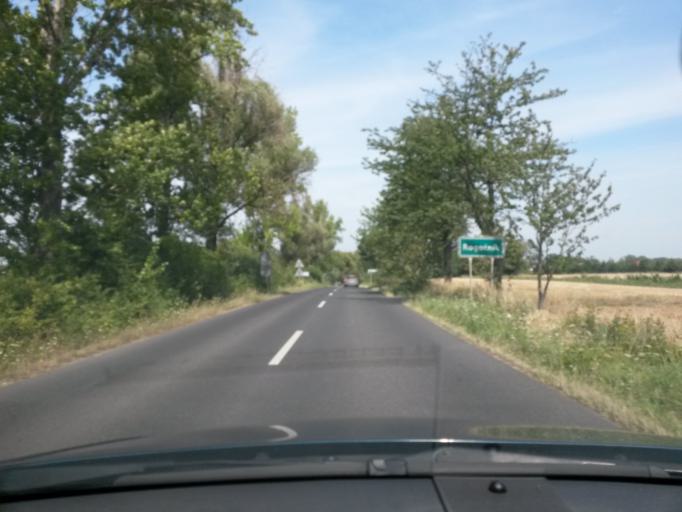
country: PL
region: Lower Silesian Voivodeship
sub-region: Powiat legnicki
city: Legnickie Pole
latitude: 51.1669
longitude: 16.3330
